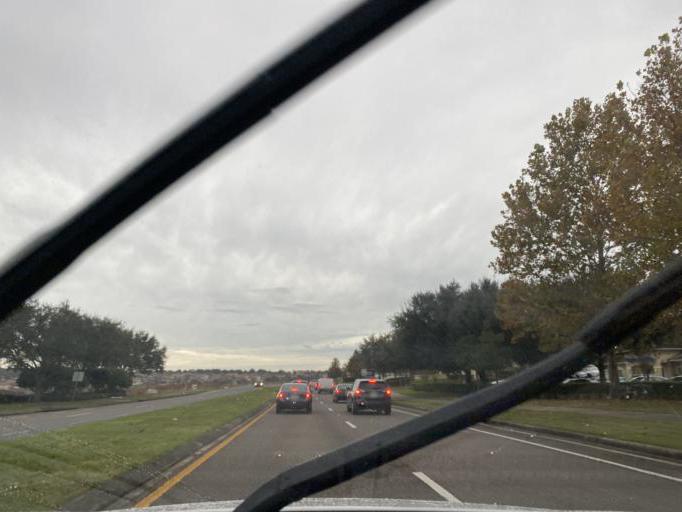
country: US
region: Florida
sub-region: Lake County
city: Clermont
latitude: 28.5227
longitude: -81.7281
